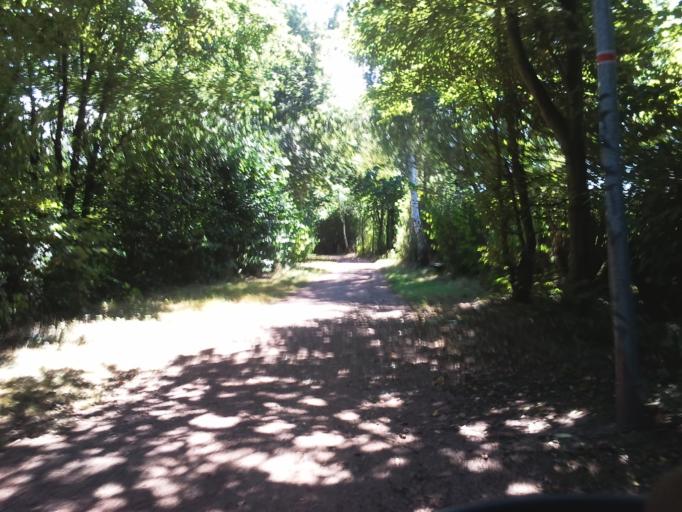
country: DE
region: Lower Saxony
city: Nienburg
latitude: 52.6675
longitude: 9.2325
